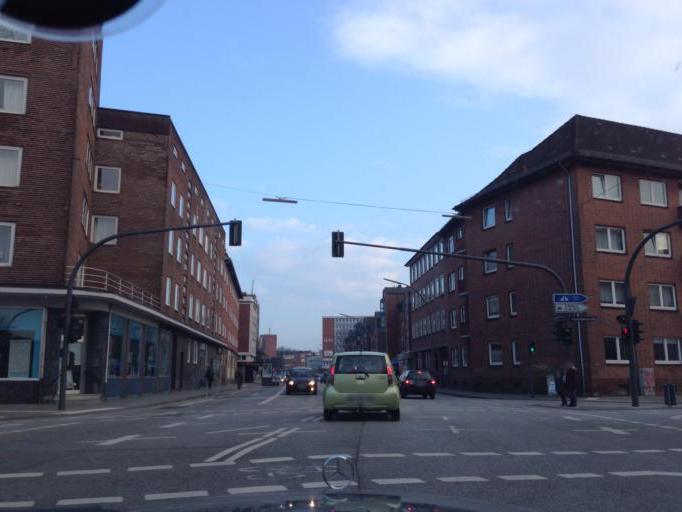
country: DE
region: Hamburg
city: Bergedorf
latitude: 53.4874
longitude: 10.2106
